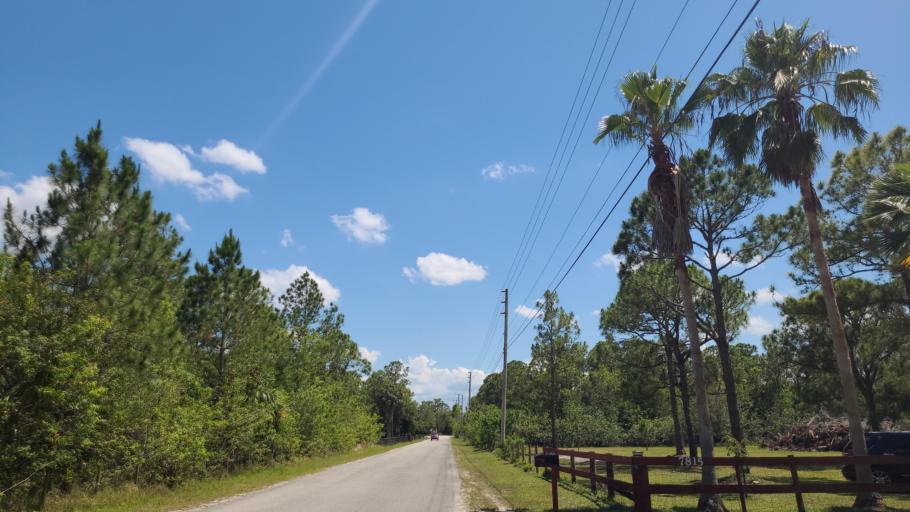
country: US
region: Florida
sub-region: Indian River County
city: Fellsmere
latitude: 27.7383
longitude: -80.5936
